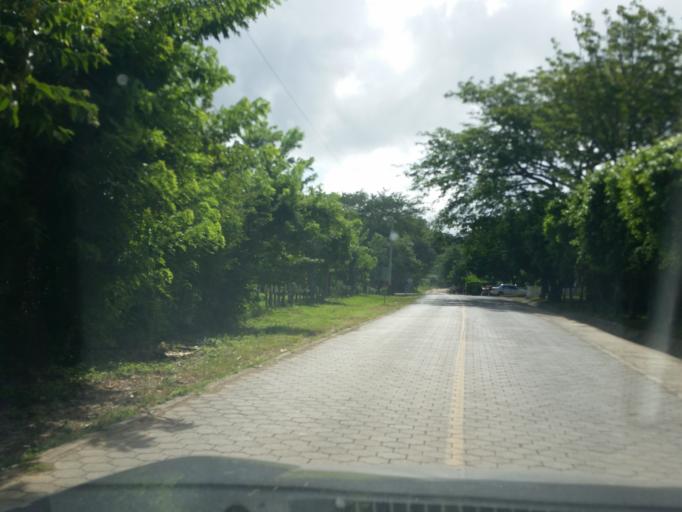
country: NI
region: Rivas
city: San Juan del Sur
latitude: 11.2452
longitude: -85.8460
